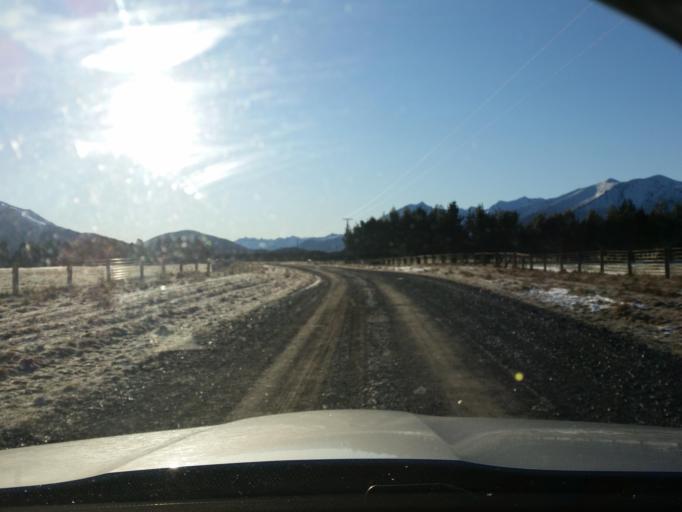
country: NZ
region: Southland
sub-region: Southland District
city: Te Anau
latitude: -45.3492
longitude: 168.1426
